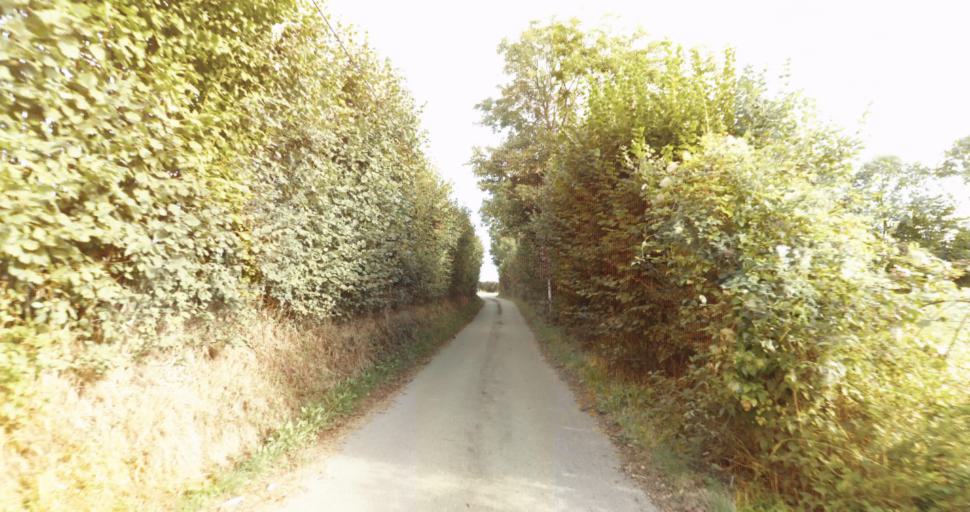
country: FR
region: Lower Normandy
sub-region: Departement de l'Orne
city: Gace
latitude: 48.6998
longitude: 0.3303
